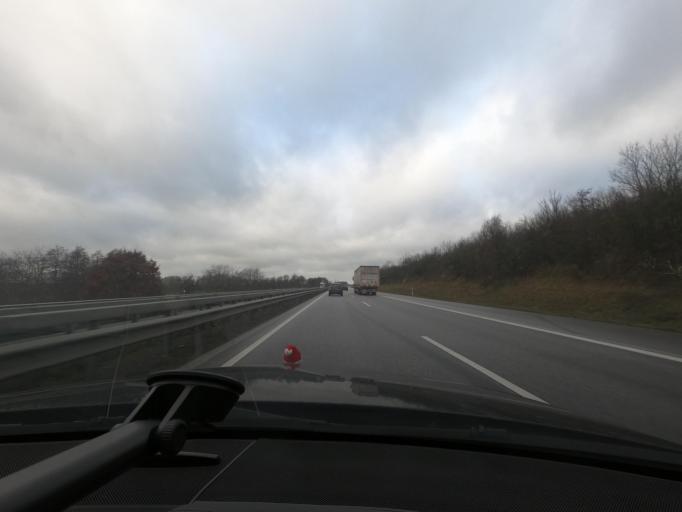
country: DE
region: Schleswig-Holstein
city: Bokel
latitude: 54.2394
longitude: 9.8226
